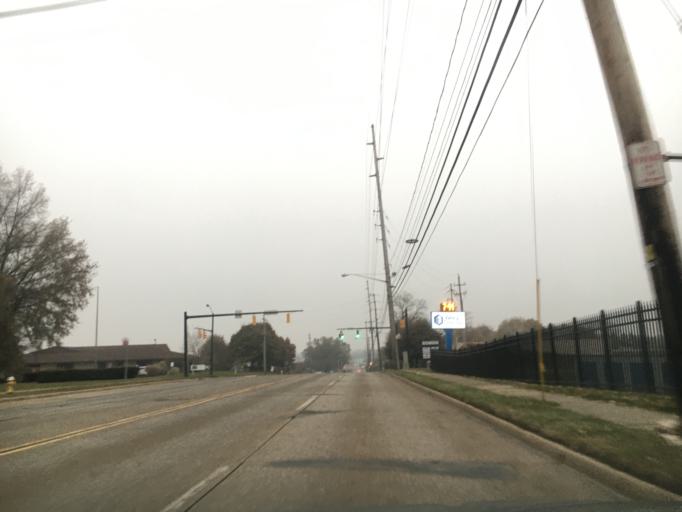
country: US
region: Ohio
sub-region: Summit County
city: Cuyahoga Falls
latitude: 41.1084
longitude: -81.4872
